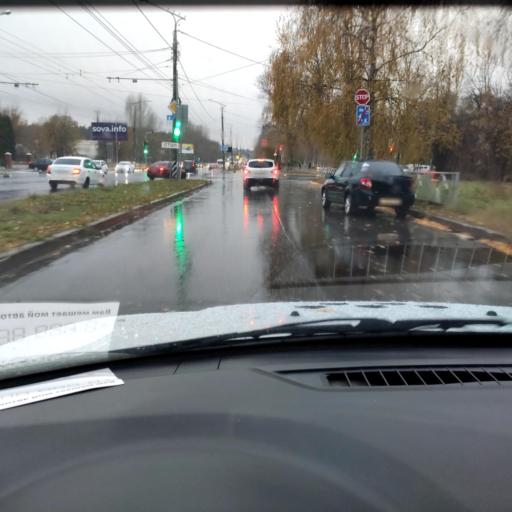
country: RU
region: Samara
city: Tol'yatti
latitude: 53.5003
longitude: 49.4155
